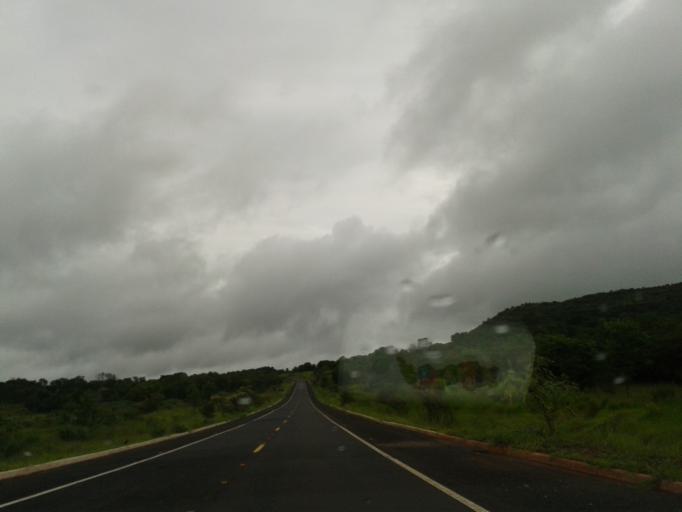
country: BR
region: Minas Gerais
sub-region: Santa Vitoria
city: Santa Vitoria
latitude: -19.2184
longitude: -50.0208
